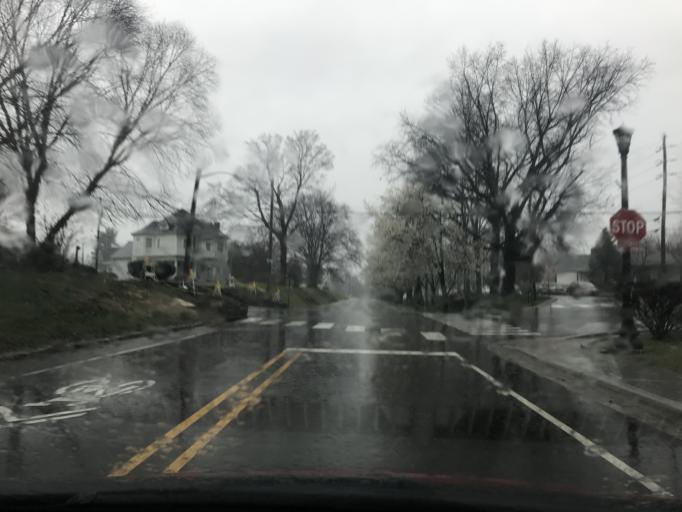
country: US
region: Indiana
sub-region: Clark County
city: Clarksville
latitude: 38.2847
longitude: -85.7620
